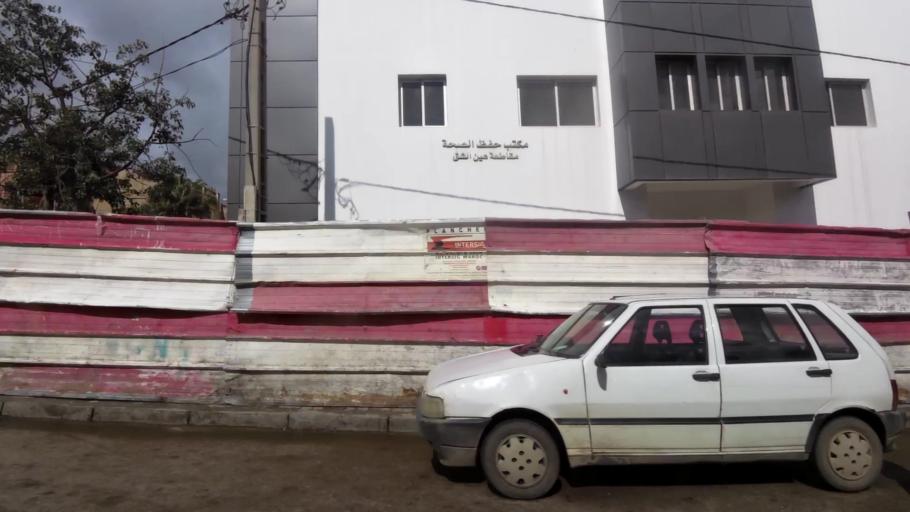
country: MA
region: Grand Casablanca
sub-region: Nouaceur
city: Bouskoura
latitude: 33.5086
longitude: -7.6574
